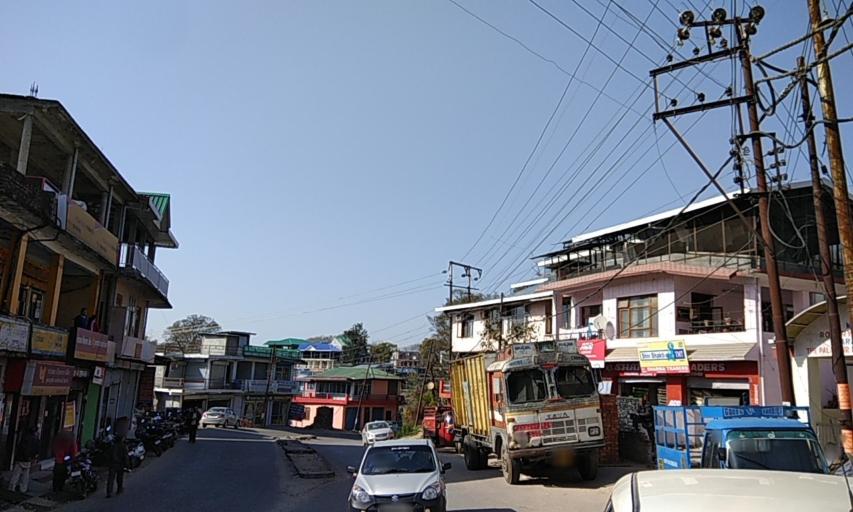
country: IN
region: Himachal Pradesh
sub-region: Kangra
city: Palampur
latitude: 32.0821
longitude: 76.5132
